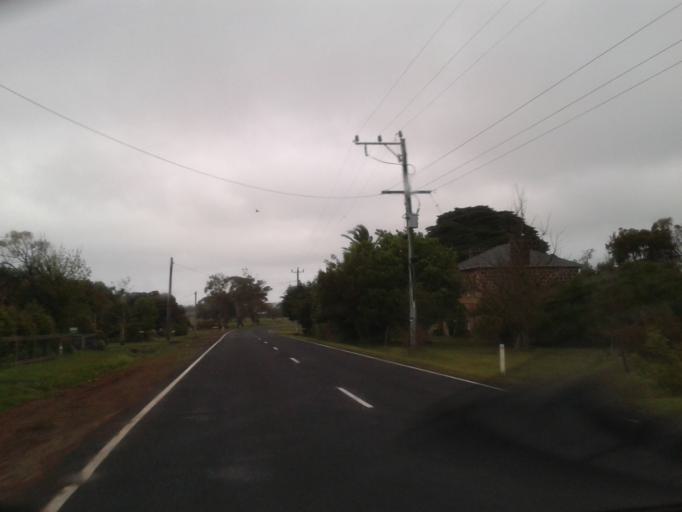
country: AU
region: Victoria
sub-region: Glenelg
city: Portland
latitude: -38.3402
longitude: 141.5746
